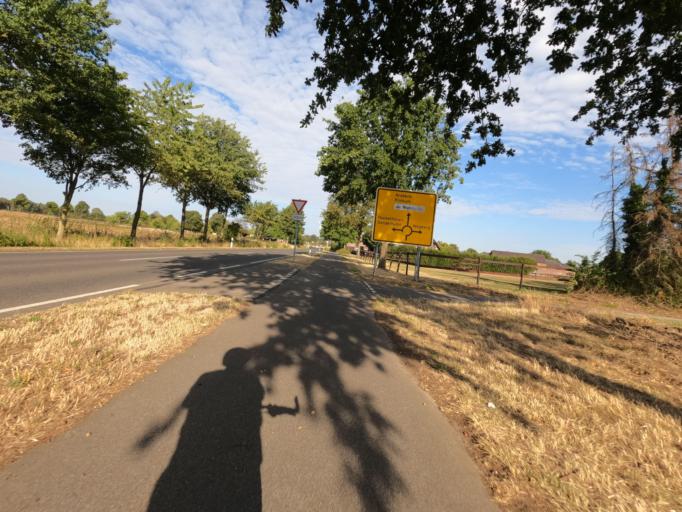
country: DE
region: North Rhine-Westphalia
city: Wegberg
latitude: 51.1154
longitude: 6.2485
